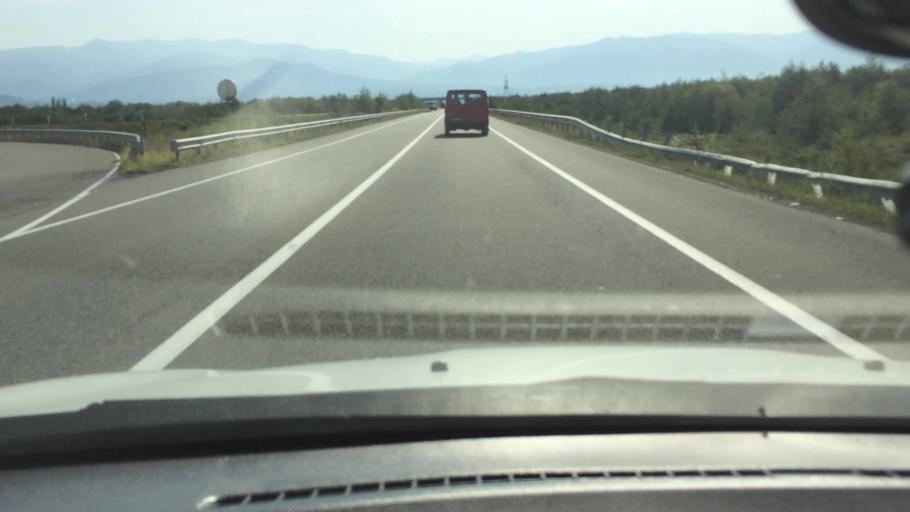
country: GE
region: Ajaria
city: Ochkhamuri
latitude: 41.8969
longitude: 41.7993
